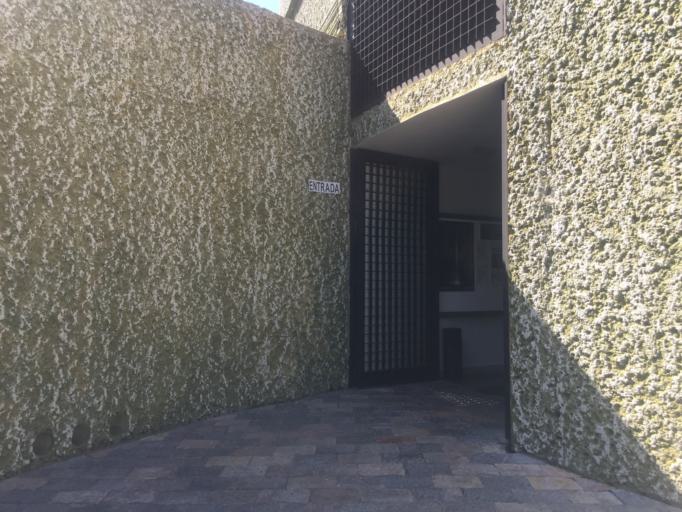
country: MX
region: Morelos
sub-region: Miacatlan
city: Xochicalco (Cirenio Longares)
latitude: 18.8021
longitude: -99.2908
